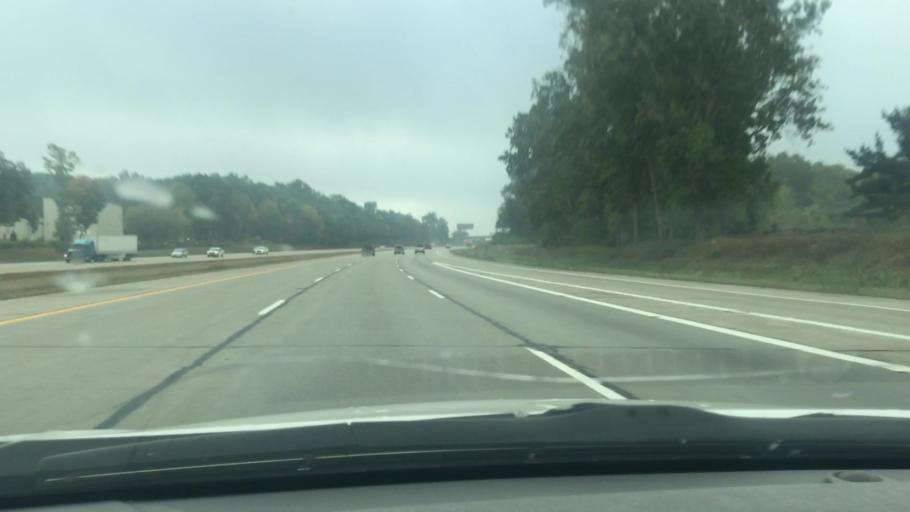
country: US
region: Michigan
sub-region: Livingston County
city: Howell
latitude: 42.6038
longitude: -83.9534
